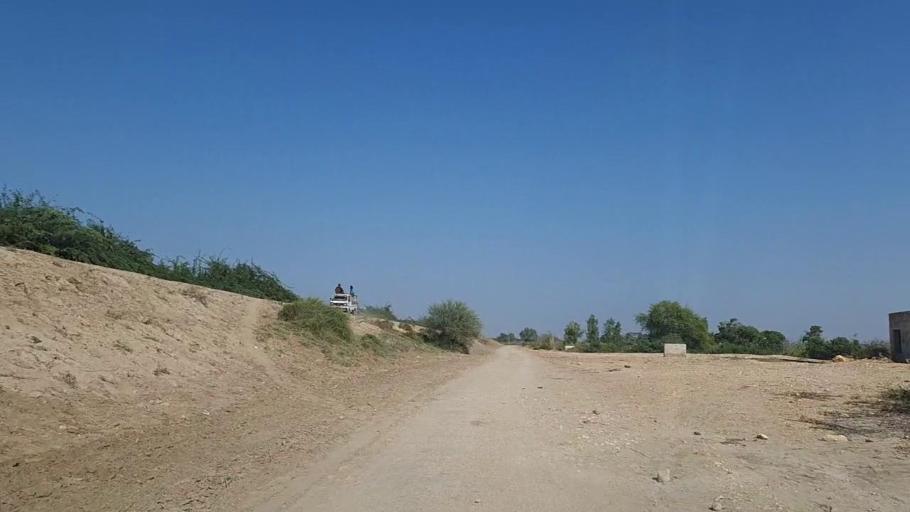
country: PK
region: Sindh
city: Thatta
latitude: 24.5842
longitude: 68.0342
